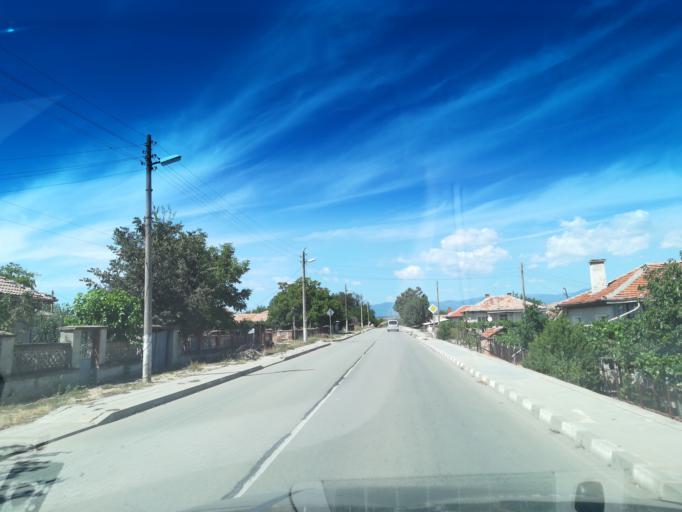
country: BG
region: Plovdiv
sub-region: Obshtina Suedinenie
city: Suedinenie
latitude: 42.3719
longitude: 24.5919
